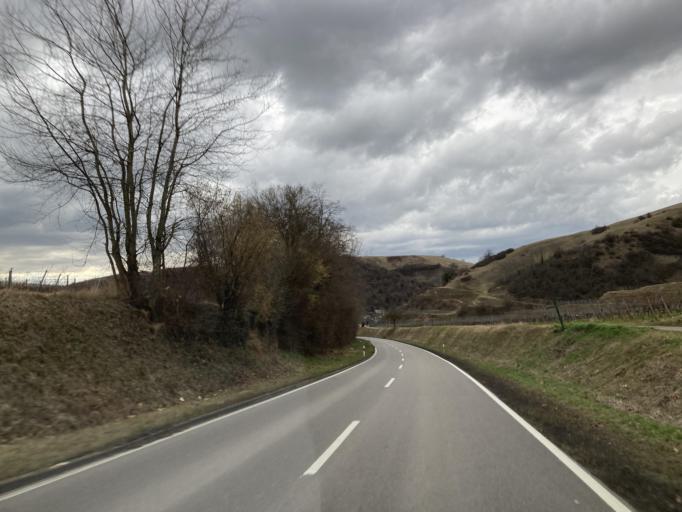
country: DE
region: Baden-Wuerttemberg
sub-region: Freiburg Region
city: Botzingen
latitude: 48.0886
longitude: 7.6888
